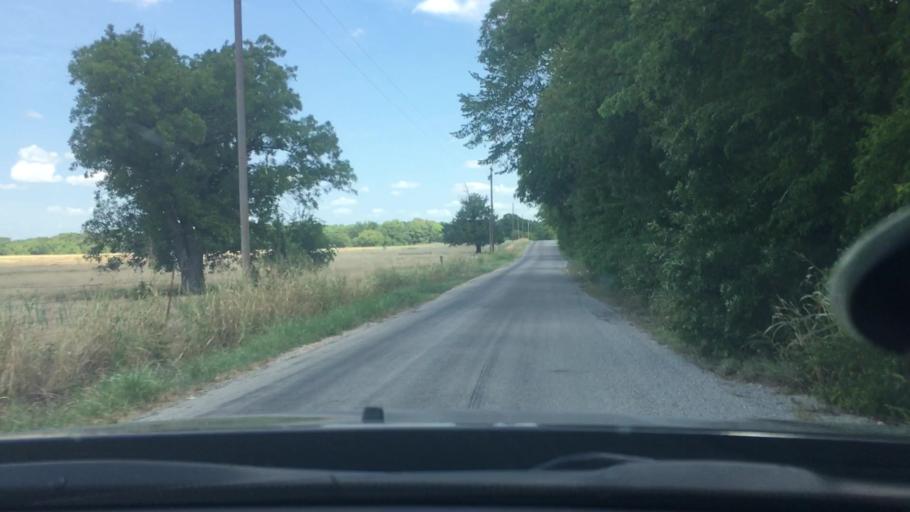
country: US
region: Oklahoma
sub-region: Love County
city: Marietta
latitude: 33.9980
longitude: -97.1870
